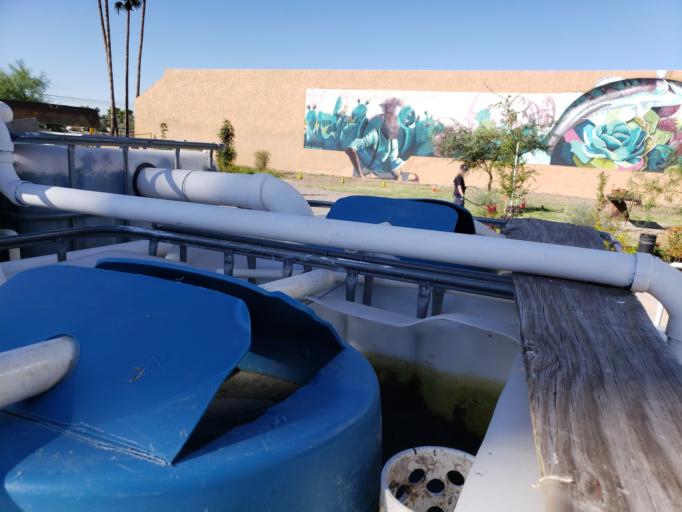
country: US
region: Arizona
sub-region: Maricopa County
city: Phoenix
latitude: 33.5102
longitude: -112.0942
